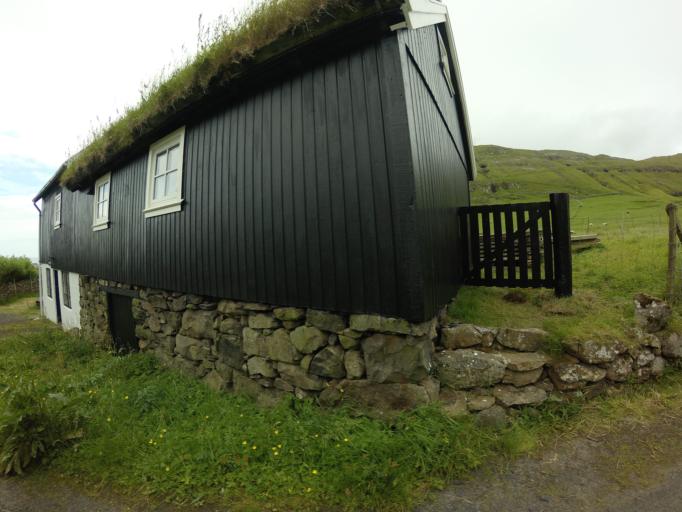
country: FO
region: Sandoy
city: Sandur
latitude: 61.7845
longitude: -6.6796
